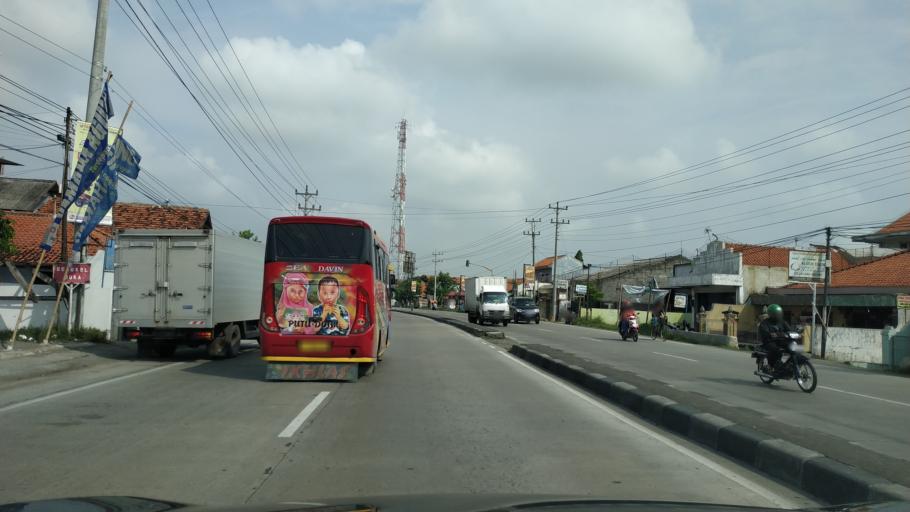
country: ID
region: Central Java
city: Bulakamba
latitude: -6.8735
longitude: 108.9460
